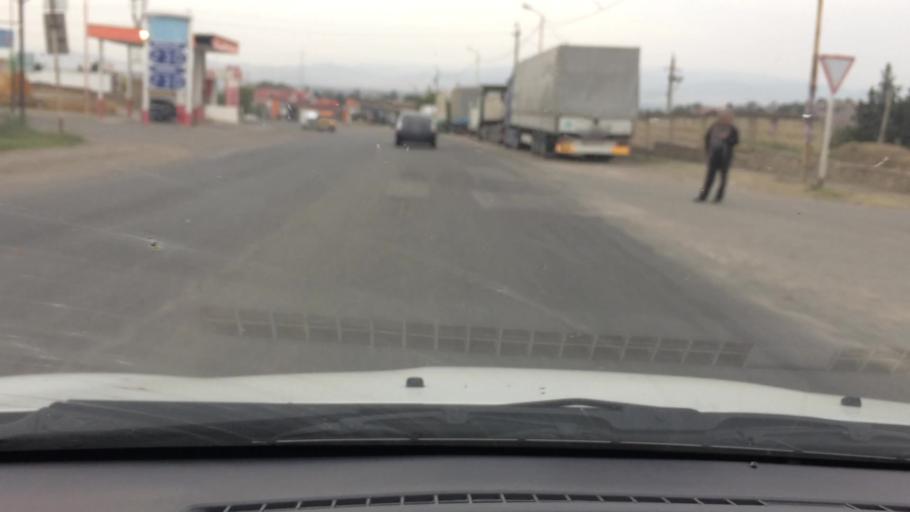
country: GE
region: Kvemo Kartli
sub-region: Marneuli
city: Marneuli
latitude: 41.4961
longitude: 44.8022
